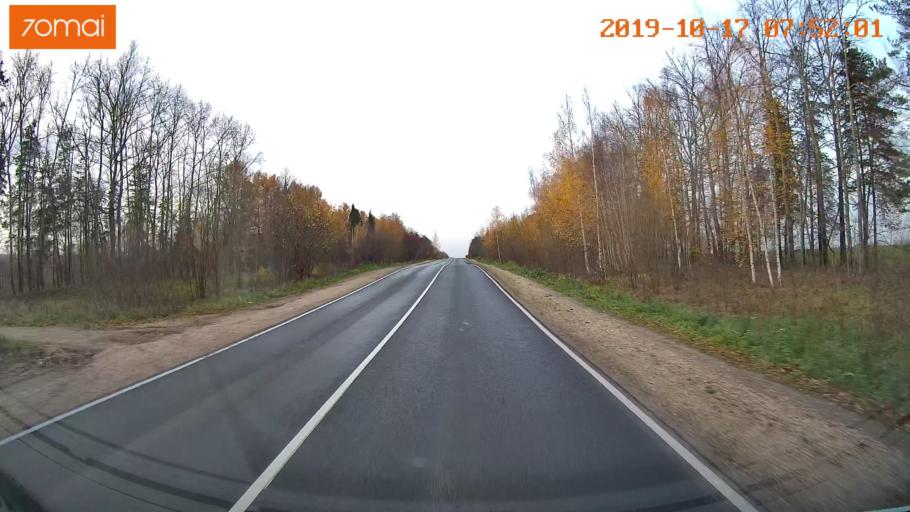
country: RU
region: Vladimir
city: Yur'yev-Pol'skiy
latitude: 56.4768
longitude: 39.6475
